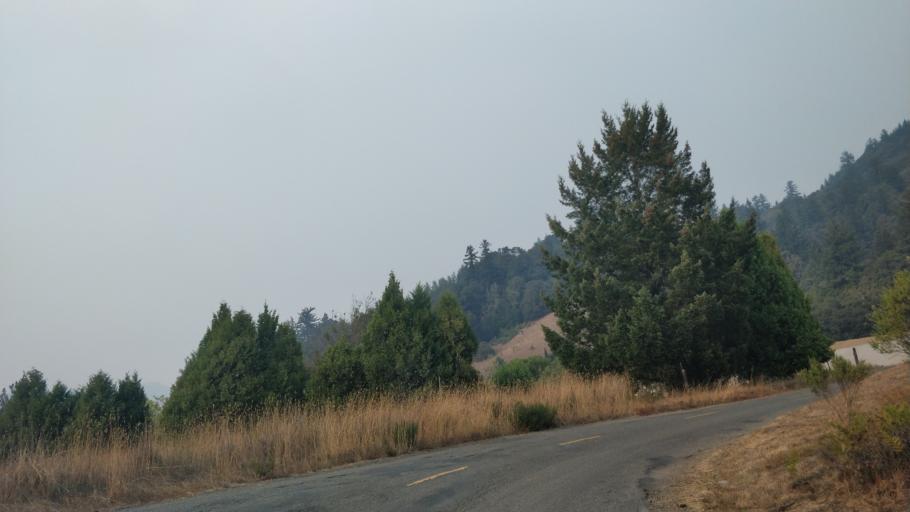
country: US
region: California
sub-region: Humboldt County
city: Rio Dell
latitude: 40.2458
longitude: -124.1244
